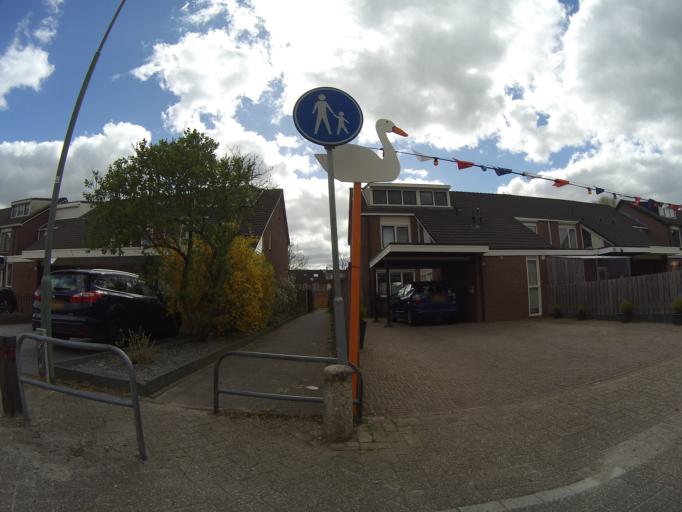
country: NL
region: Utrecht
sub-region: Gemeente Bunschoten
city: Spakenburg
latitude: 52.2415
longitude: 5.3635
